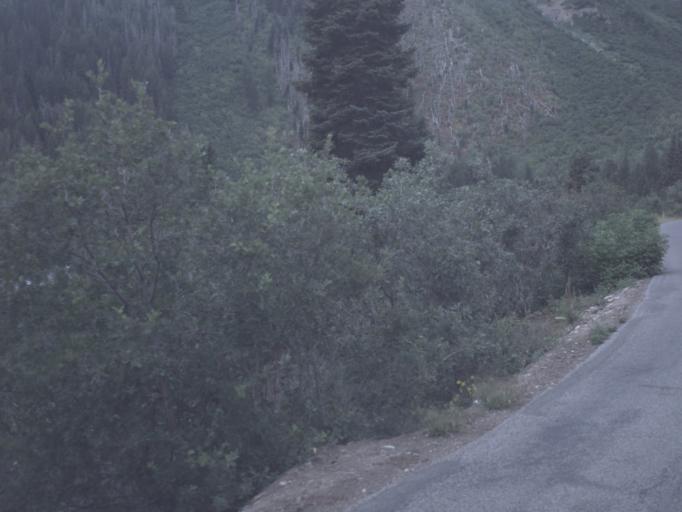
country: US
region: Utah
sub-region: Utah County
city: Lindon
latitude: 40.4079
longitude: -111.6039
